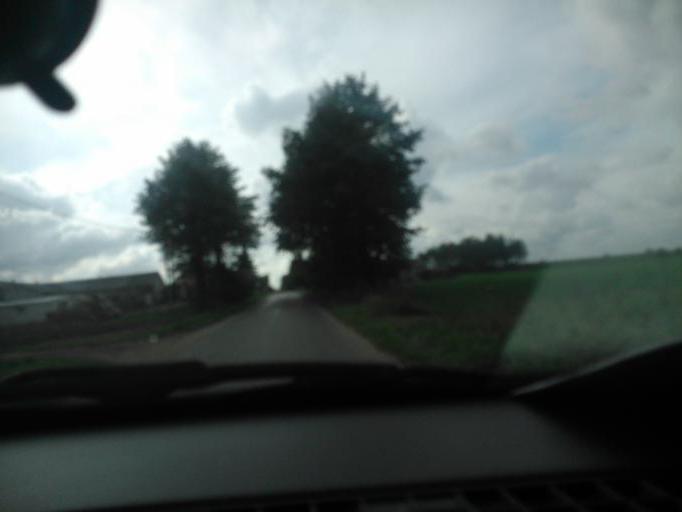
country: PL
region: Kujawsko-Pomorskie
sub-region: Powiat brodnicki
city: Swiedziebnia
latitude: 53.2088
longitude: 19.4784
